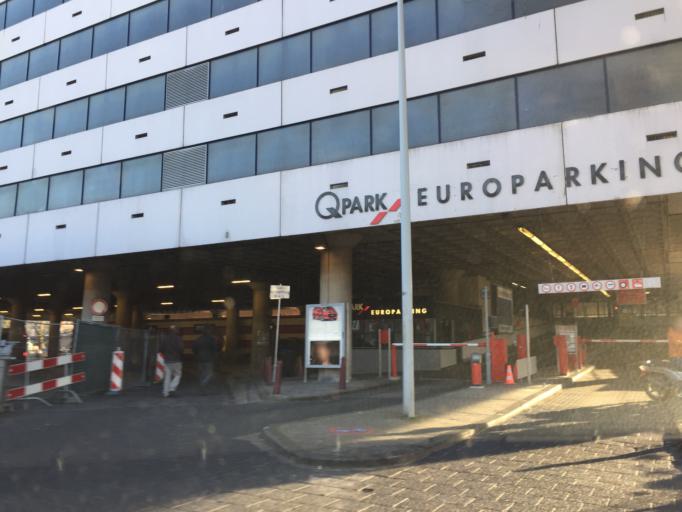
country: NL
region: North Holland
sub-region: Gemeente Amsterdam
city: Amsterdam
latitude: 52.3701
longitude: 4.8769
